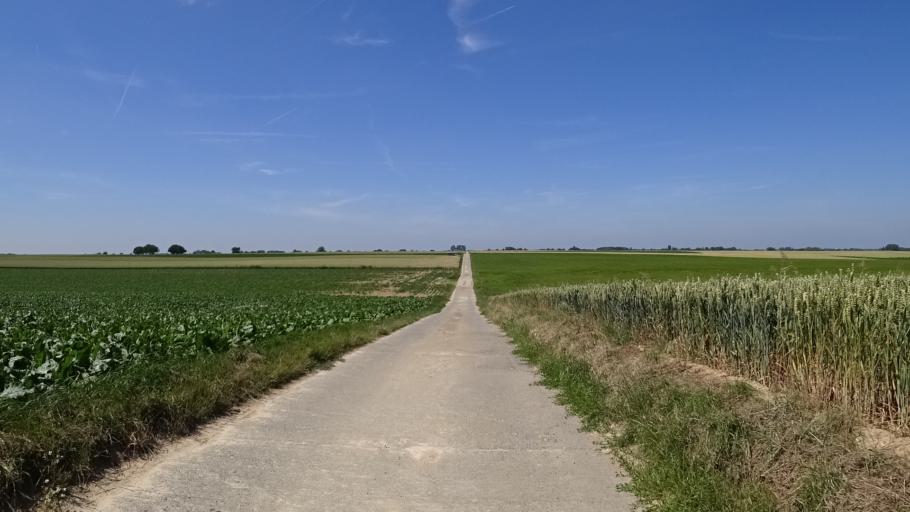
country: BE
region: Wallonia
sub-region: Province du Brabant Wallon
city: Perwez
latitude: 50.6577
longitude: 4.8451
